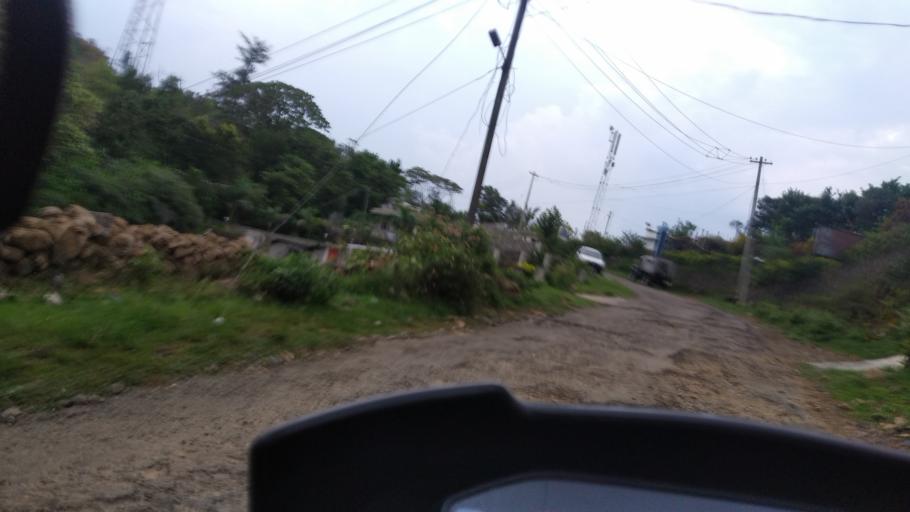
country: IN
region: Tamil Nadu
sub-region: Theni
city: Gudalur
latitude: 9.5473
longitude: 77.0354
